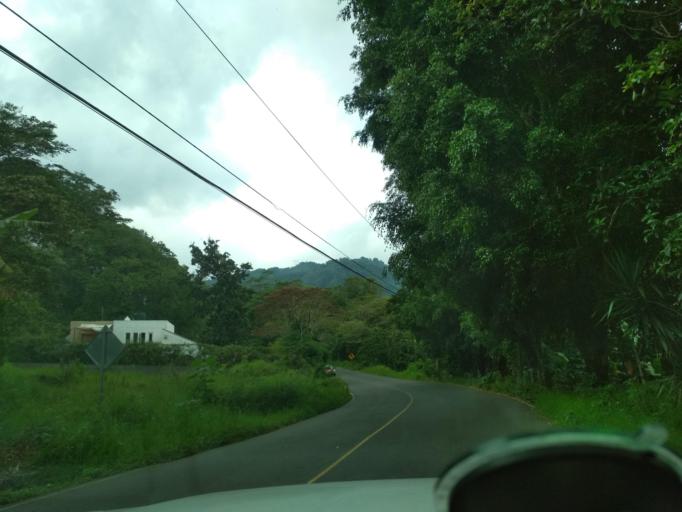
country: MX
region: Veracruz
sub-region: Jilotepec
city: El Pueblito (Garbanzal)
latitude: 19.6160
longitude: -96.9293
